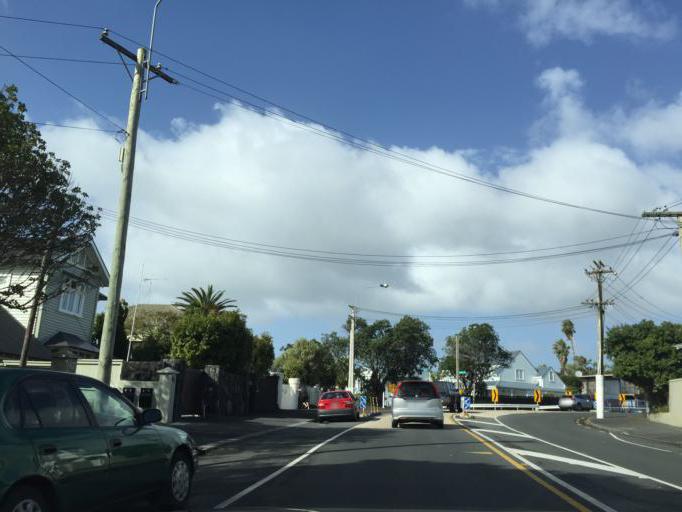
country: NZ
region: Auckland
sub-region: Auckland
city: Auckland
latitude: -36.8411
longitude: 174.7428
